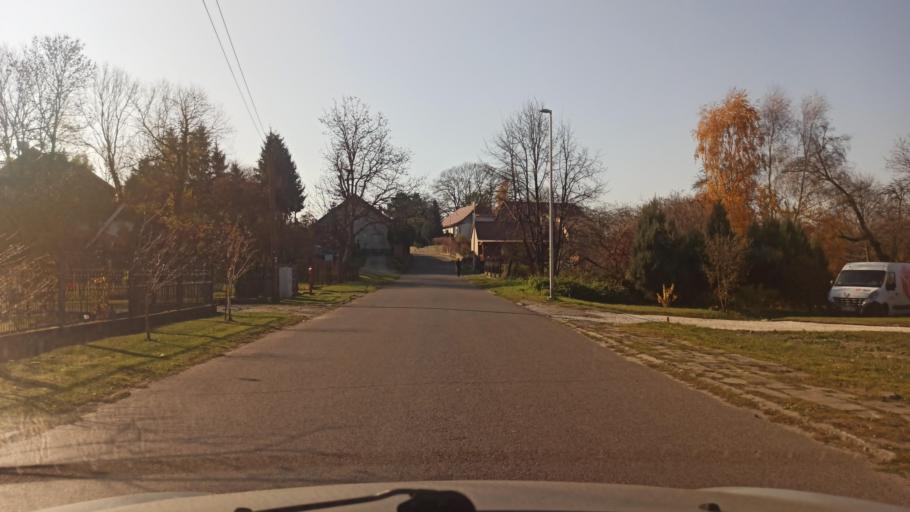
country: PL
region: Subcarpathian Voivodeship
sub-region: Powiat jaroslawski
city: Radymno
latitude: 49.9442
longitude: 22.8209
